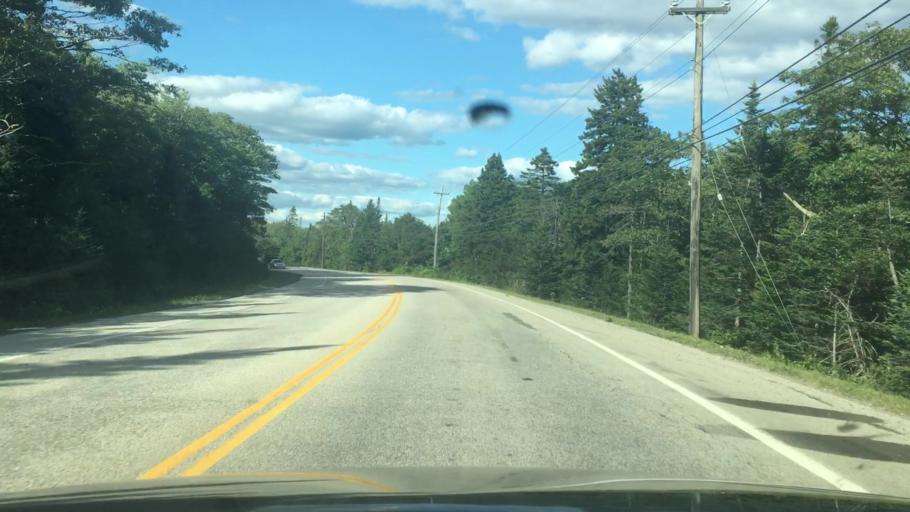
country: CA
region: Nova Scotia
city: Halifax
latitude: 44.6103
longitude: -63.6702
